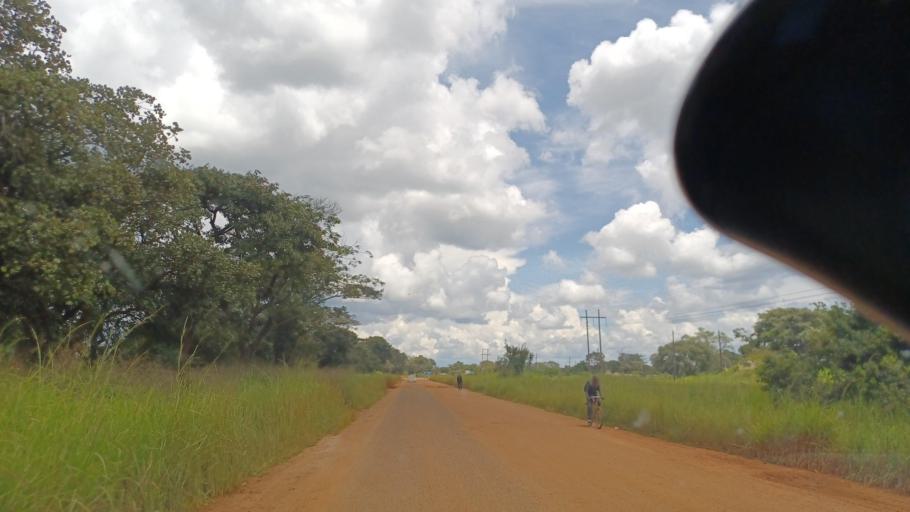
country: ZM
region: North-Western
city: Solwezi
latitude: -12.4787
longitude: 26.1985
